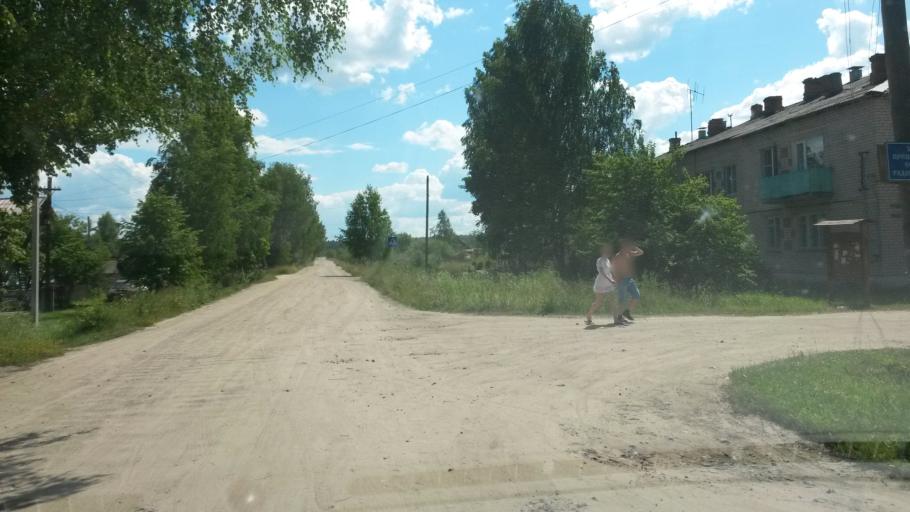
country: RU
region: Ivanovo
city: Zarechnyy
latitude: 57.4979
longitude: 42.3332
